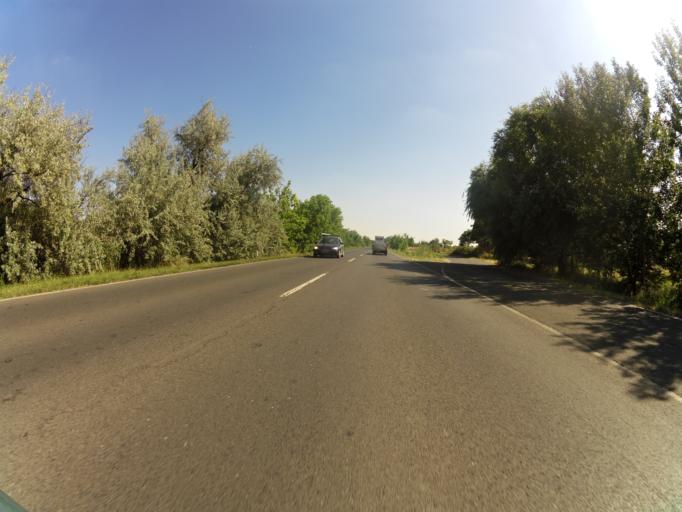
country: HU
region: Csongrad
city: Szatymaz
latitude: 46.3188
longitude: 20.0636
